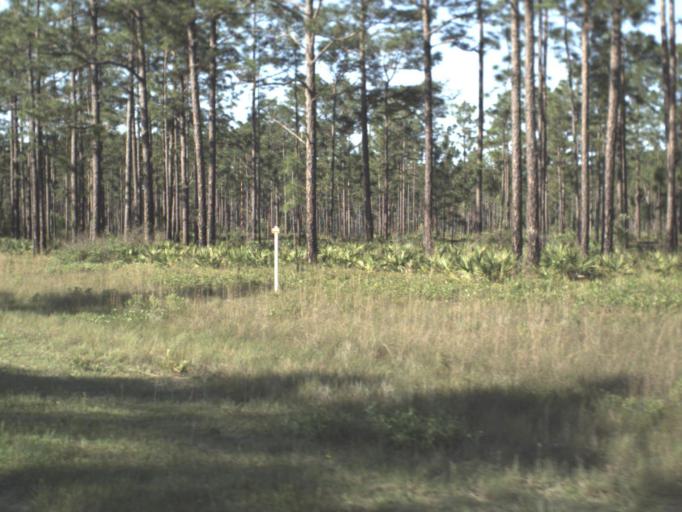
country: US
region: Florida
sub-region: Gulf County
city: Wewahitchka
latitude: 30.1190
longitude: -84.9882
